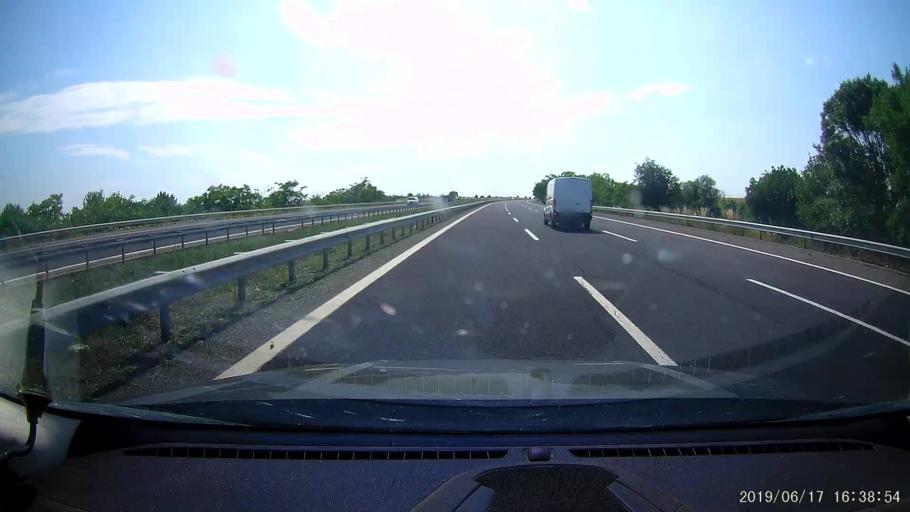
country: TR
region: Kirklareli
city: Luleburgaz
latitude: 41.4469
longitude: 27.4285
